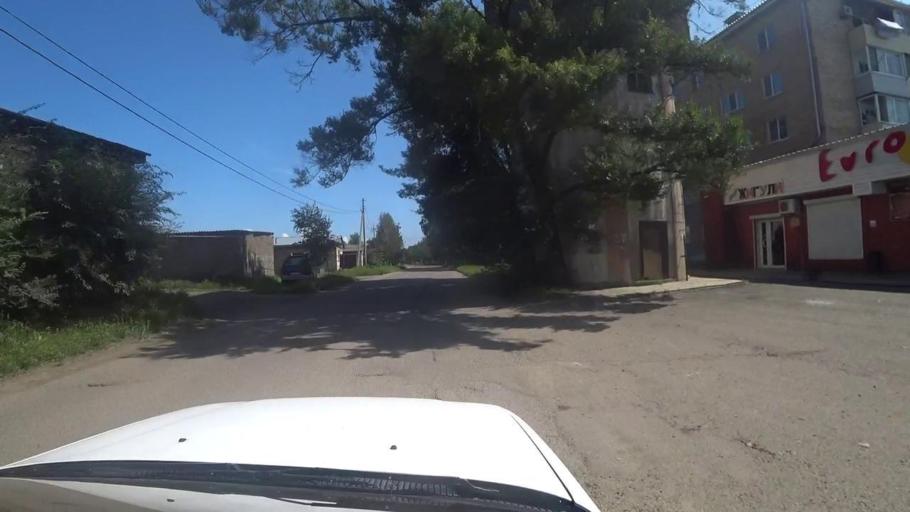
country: RU
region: Primorskiy
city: Dal'nerechensk
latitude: 45.9360
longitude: 133.7280
